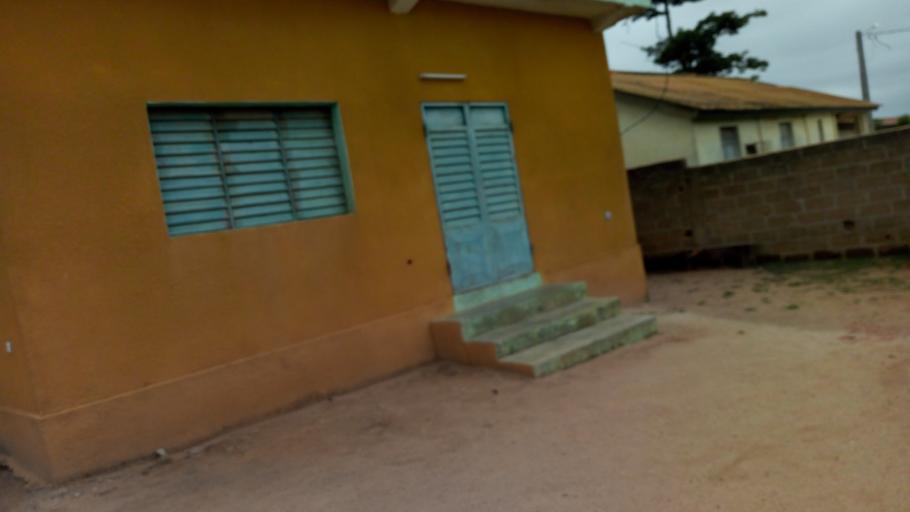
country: CI
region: Vallee du Bandama
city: Bouake
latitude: 7.7067
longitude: -5.0403
